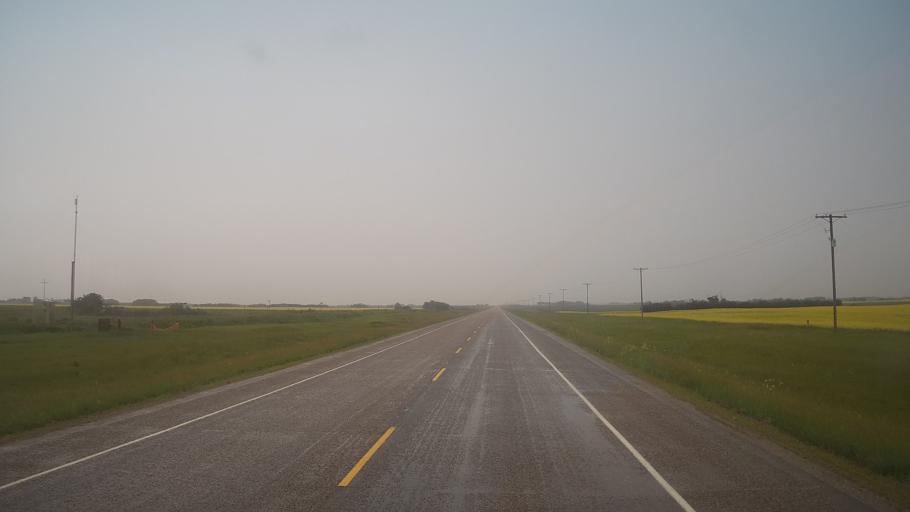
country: CA
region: Saskatchewan
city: Biggar
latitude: 52.1514
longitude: -108.2353
